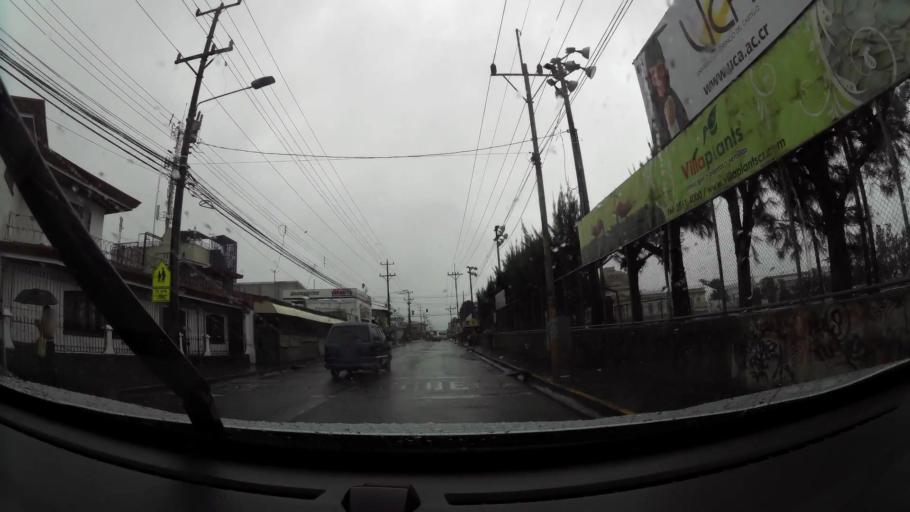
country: CR
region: Cartago
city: Cartago
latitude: 9.8634
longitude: -83.9238
